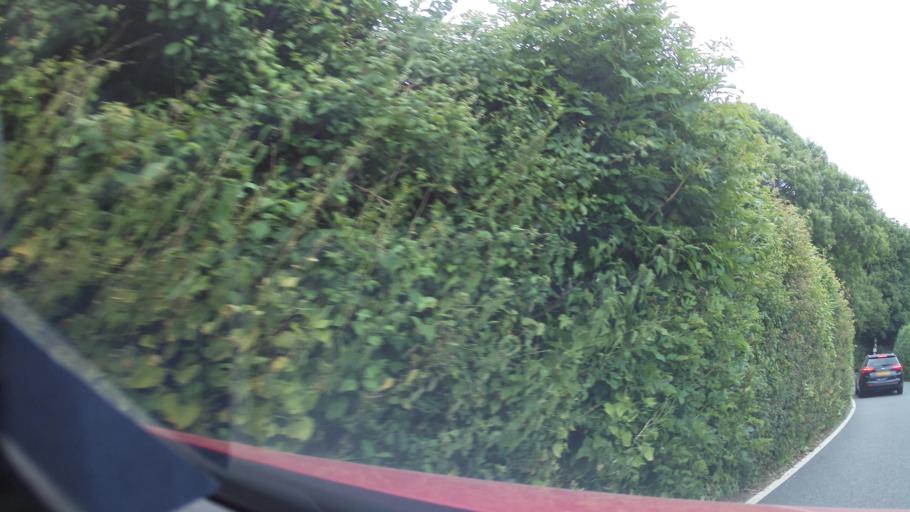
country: GB
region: England
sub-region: Devon
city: Colyton
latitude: 50.7040
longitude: -3.1000
